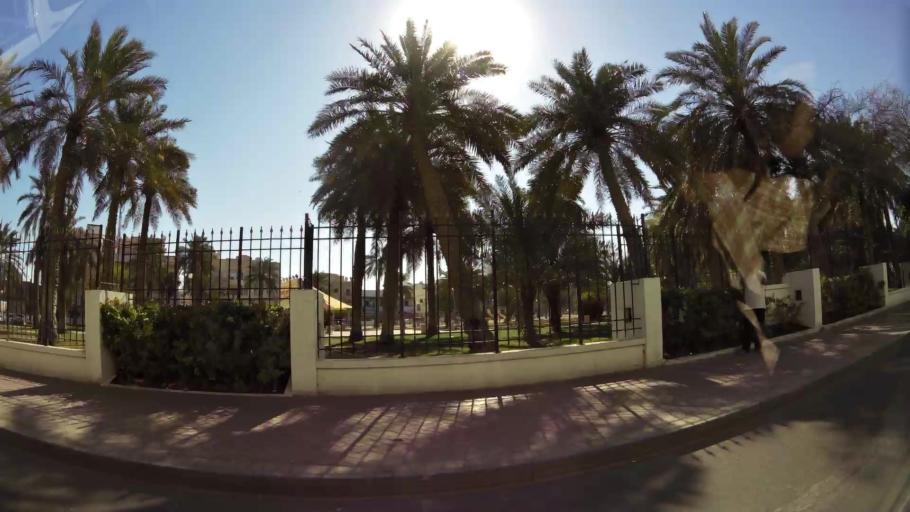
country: BH
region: Muharraq
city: Al Muharraq
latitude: 26.2604
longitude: 50.6146
